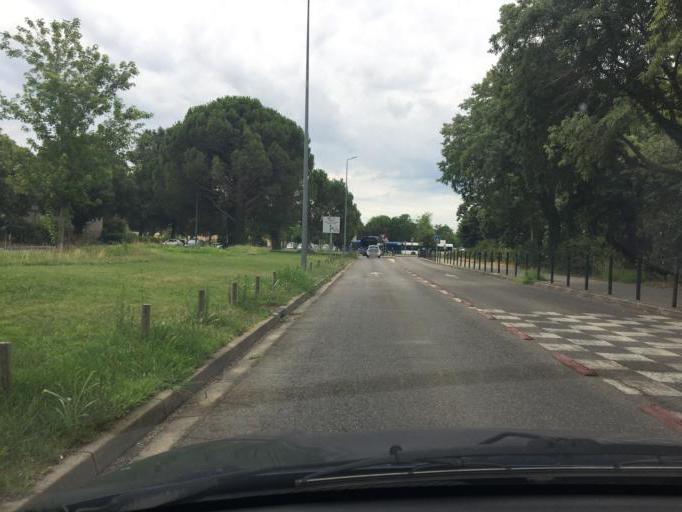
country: FR
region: Provence-Alpes-Cote d'Azur
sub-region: Departement des Bouches-du-Rhone
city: Rognonas
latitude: 43.9194
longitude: 4.8047
